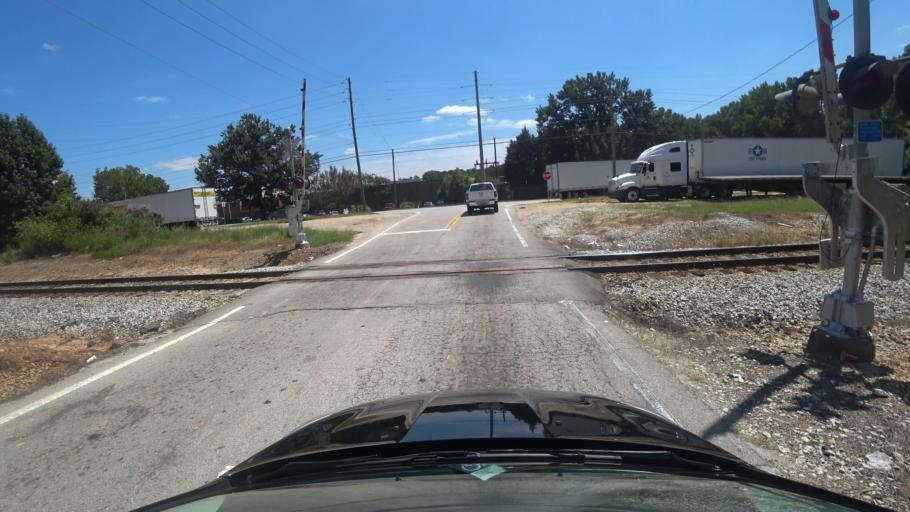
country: US
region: Georgia
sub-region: Newton County
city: Covington
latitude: 33.6134
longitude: -83.8367
